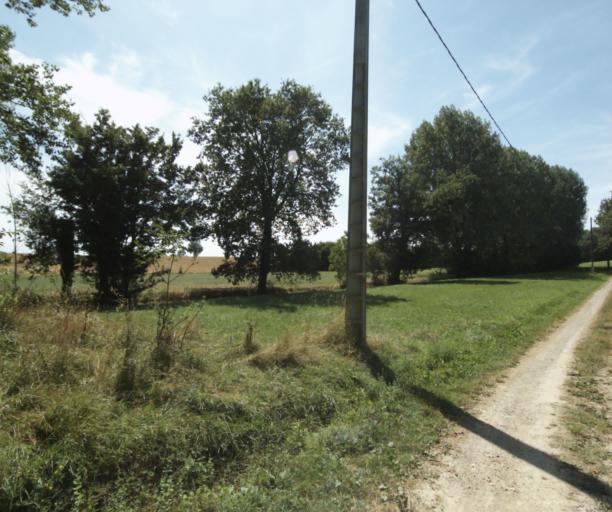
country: FR
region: Midi-Pyrenees
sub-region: Departement du Tarn
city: Puylaurens
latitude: 43.5403
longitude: 2.0204
